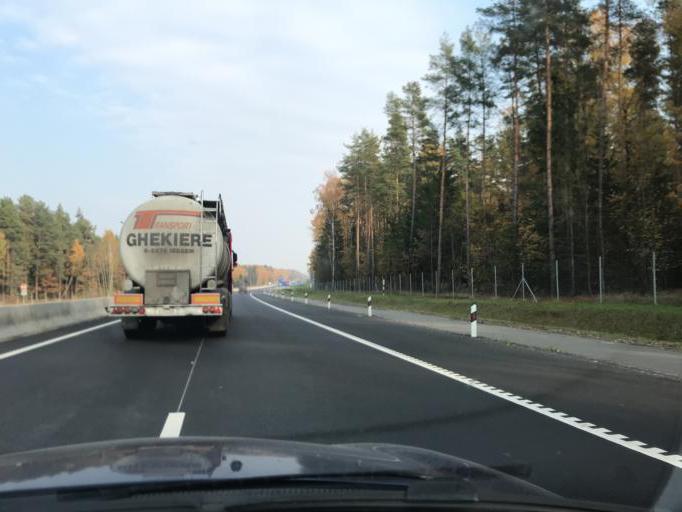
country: BY
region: Grodnenskaya
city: Shchuchin
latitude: 53.6811
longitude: 24.8469
